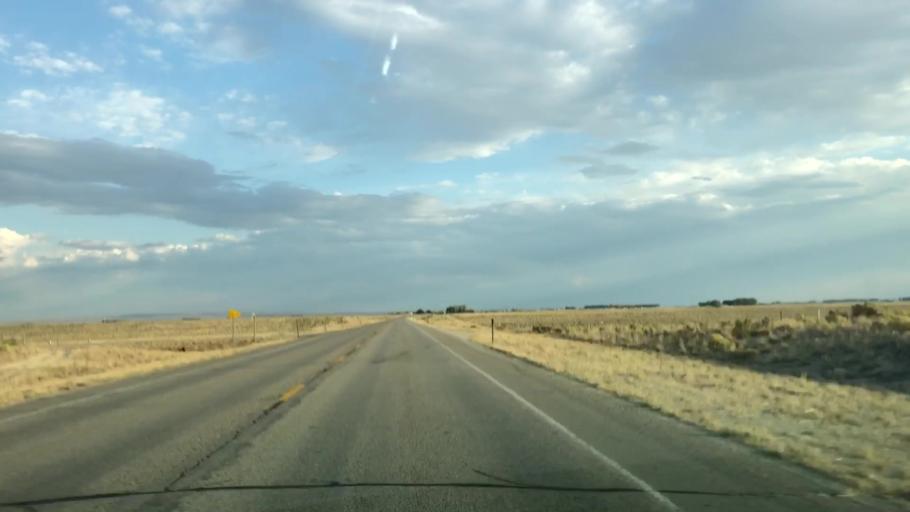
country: US
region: Wyoming
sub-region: Sweetwater County
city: North Rock Springs
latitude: 42.0947
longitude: -109.4431
